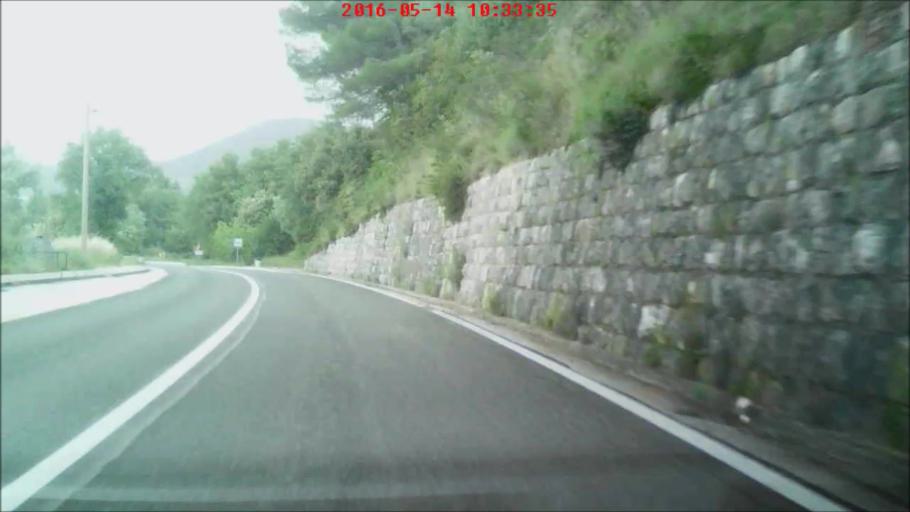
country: HR
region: Dubrovacko-Neretvanska
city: Podgora
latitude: 42.7747
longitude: 17.8881
